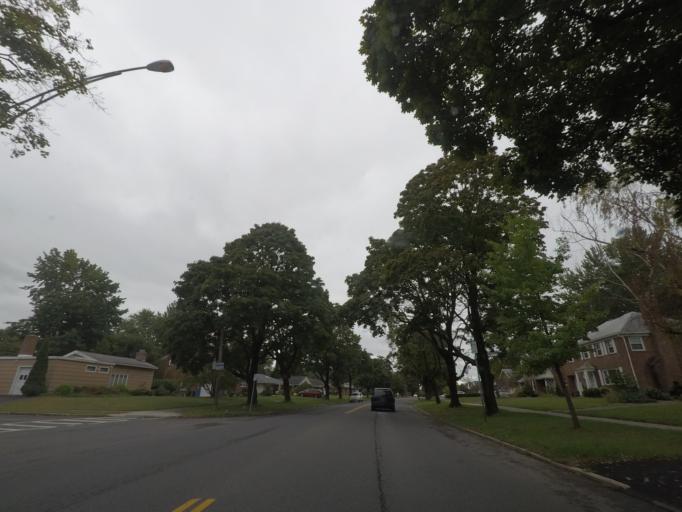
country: US
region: New York
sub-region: Albany County
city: Delmar
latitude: 42.6527
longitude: -73.8070
